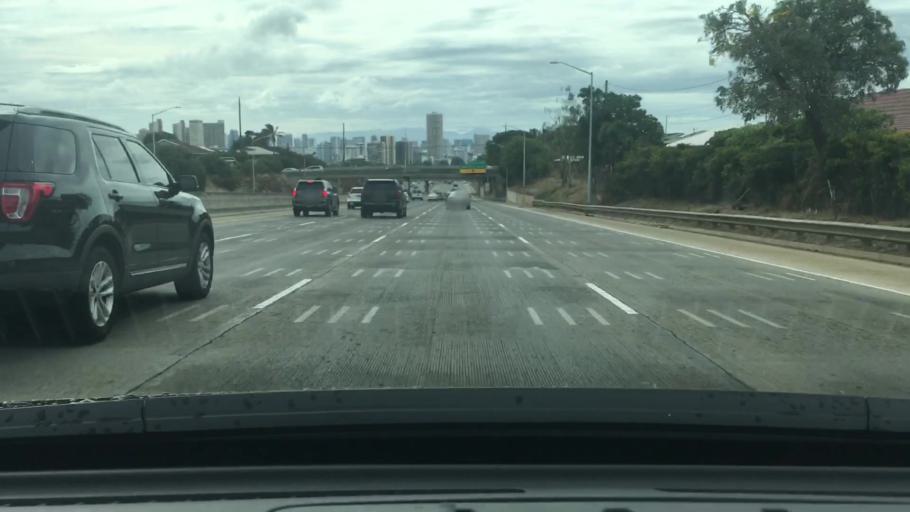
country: US
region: Hawaii
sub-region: Honolulu County
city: Honolulu
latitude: 21.2825
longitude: -157.8043
